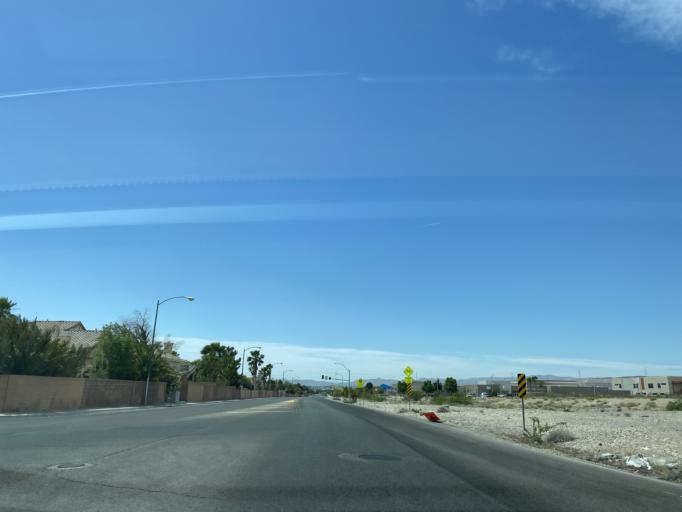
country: US
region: Nevada
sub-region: Clark County
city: Spring Valley
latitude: 36.1223
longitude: -115.2700
